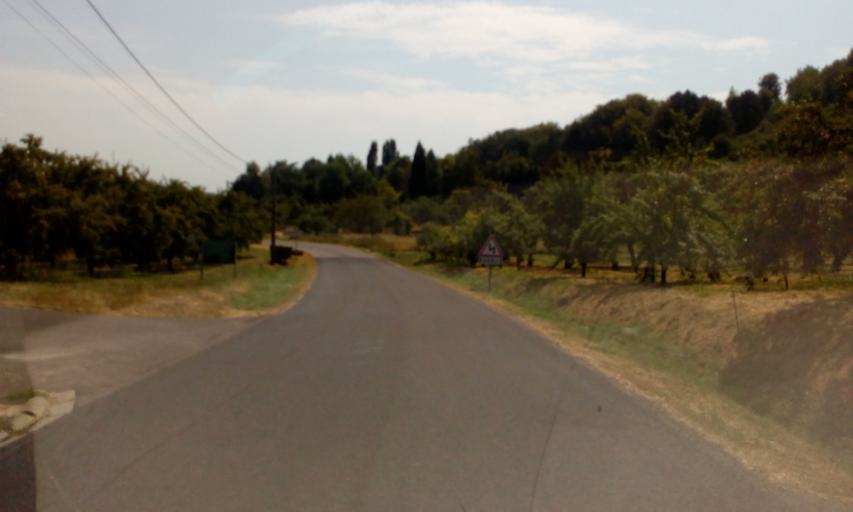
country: FR
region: Lorraine
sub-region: Departement de la Meuse
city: Etain
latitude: 49.1371
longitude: 5.5431
